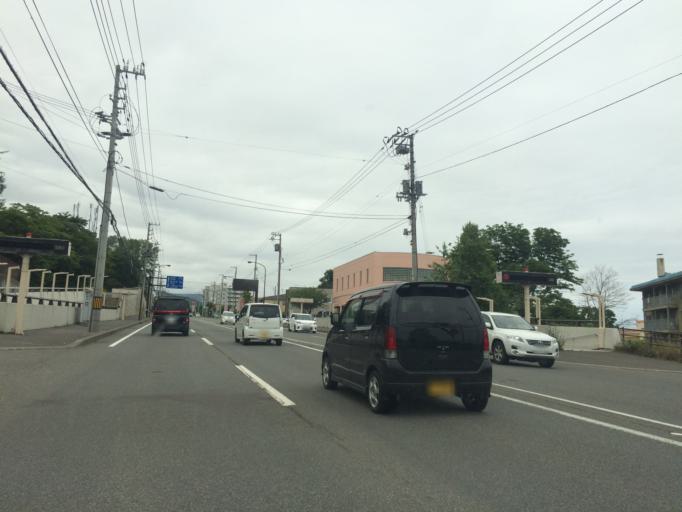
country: JP
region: Hokkaido
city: Otaru
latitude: 43.1390
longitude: 141.1614
